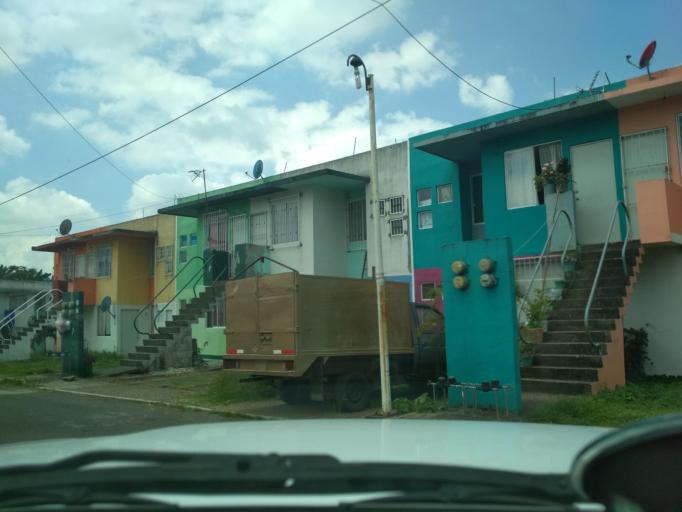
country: MX
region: Veracruz
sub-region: Fortin
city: Fraccionamiento los Alamos
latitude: 18.9281
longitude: -96.9765
